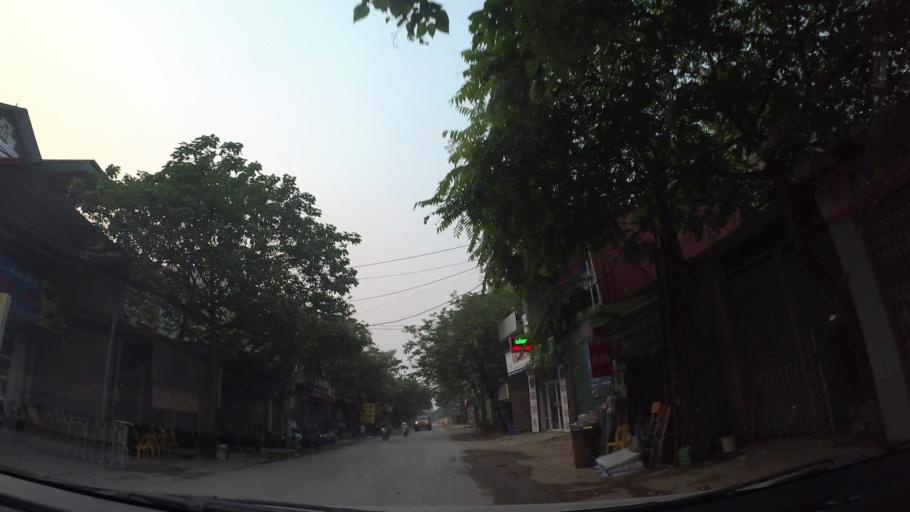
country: VN
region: Ha Noi
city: Ha Dong
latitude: 20.9923
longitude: 105.7247
